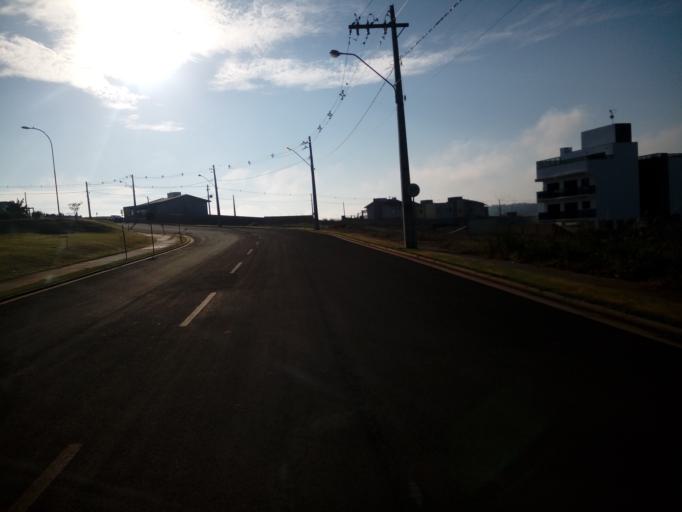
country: BR
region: Santa Catarina
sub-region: Chapeco
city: Chapeco
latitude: -27.0893
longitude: -52.7116
